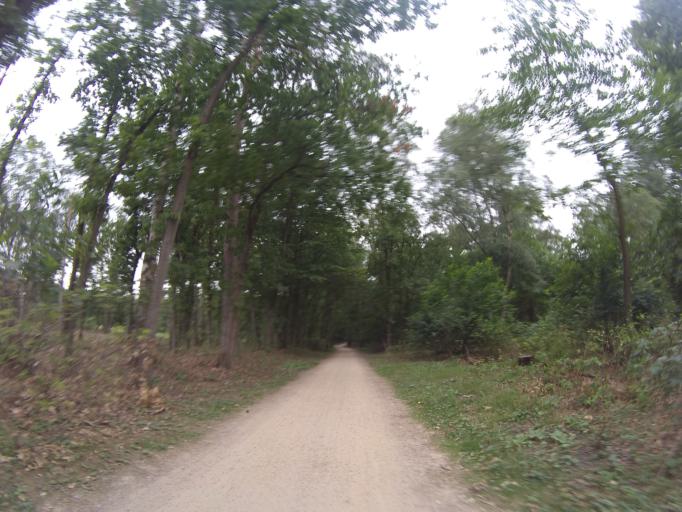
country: NL
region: North Holland
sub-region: Gemeente Bussum
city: Bussum
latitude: 52.2549
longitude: 5.1521
